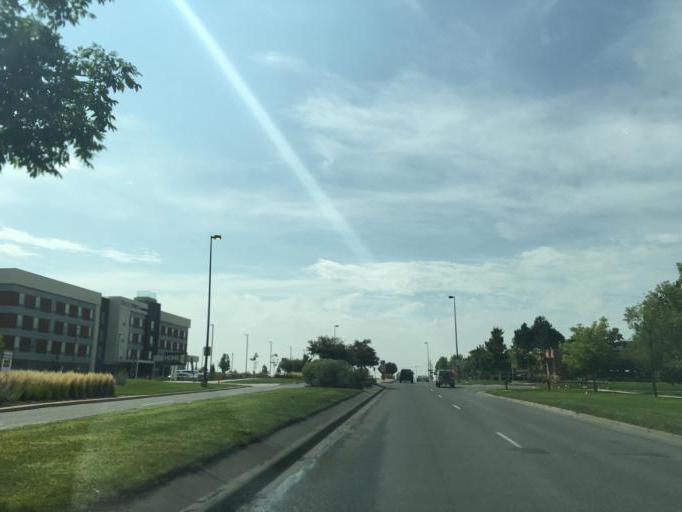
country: US
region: Colorado
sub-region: Adams County
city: Aurora
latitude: 39.8209
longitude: -104.7721
